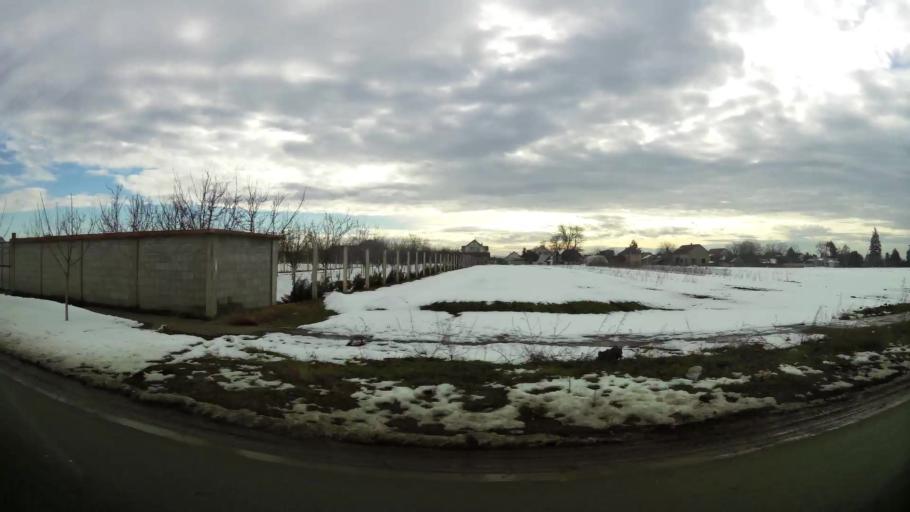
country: RS
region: Central Serbia
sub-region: Belgrade
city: Surcin
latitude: 44.7950
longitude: 20.2587
